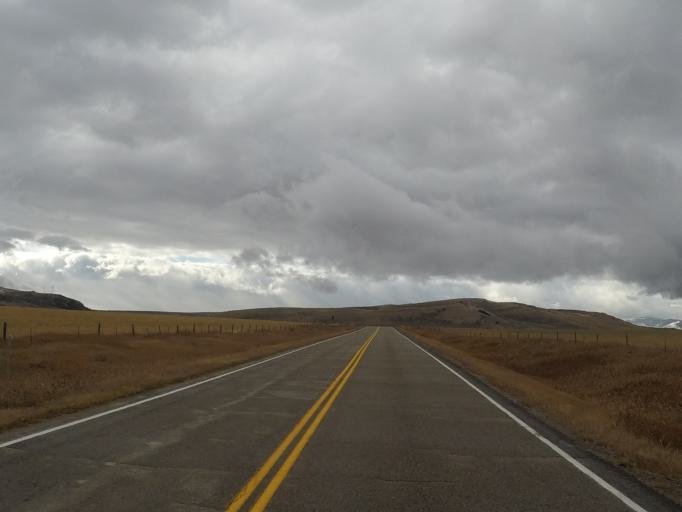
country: US
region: Montana
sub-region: Meagher County
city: White Sulphur Springs
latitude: 46.3383
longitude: -110.7895
